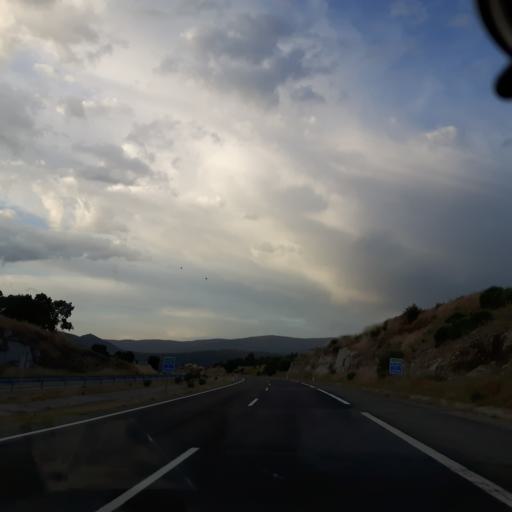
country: ES
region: Castille and Leon
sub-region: Provincia de Salamanca
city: Nava de Bejar
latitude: 40.4721
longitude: -5.6821
